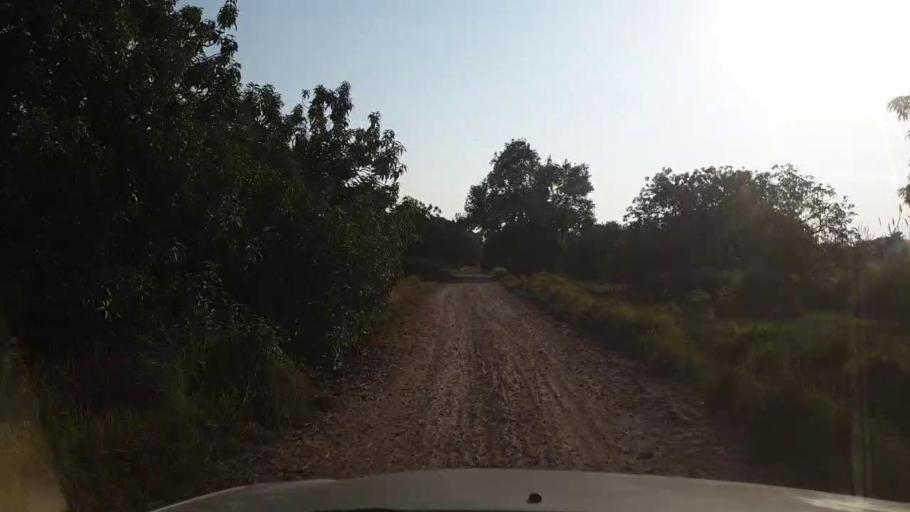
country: PK
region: Sindh
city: Tando Muhammad Khan
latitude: 25.1221
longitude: 68.5521
